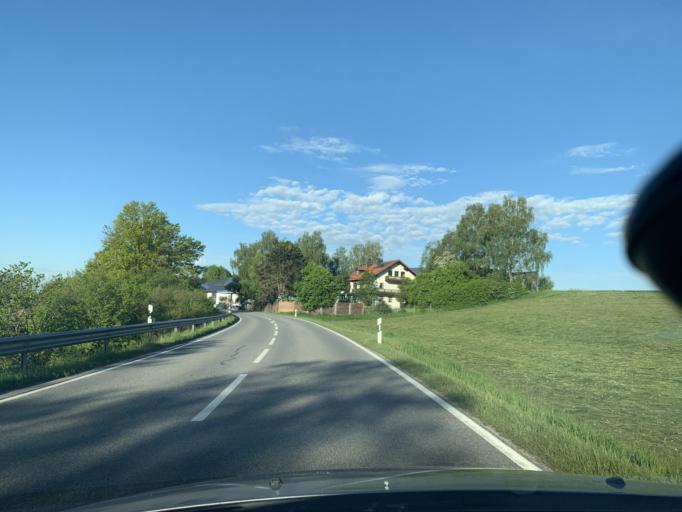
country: DE
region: Bavaria
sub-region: Lower Bavaria
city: Schalkham
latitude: 48.4777
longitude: 12.3867
